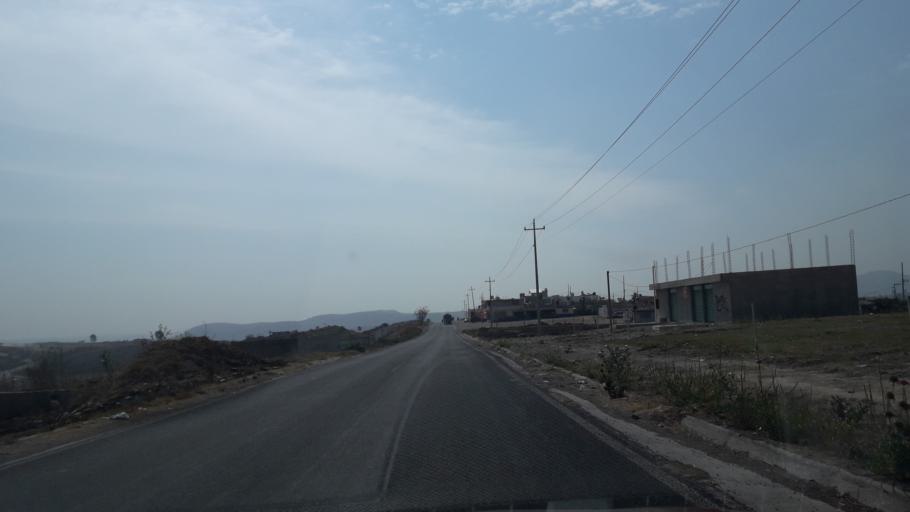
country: MX
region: Puebla
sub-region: Puebla
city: El Capulo (La Quebradora)
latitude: 18.9363
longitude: -98.2689
